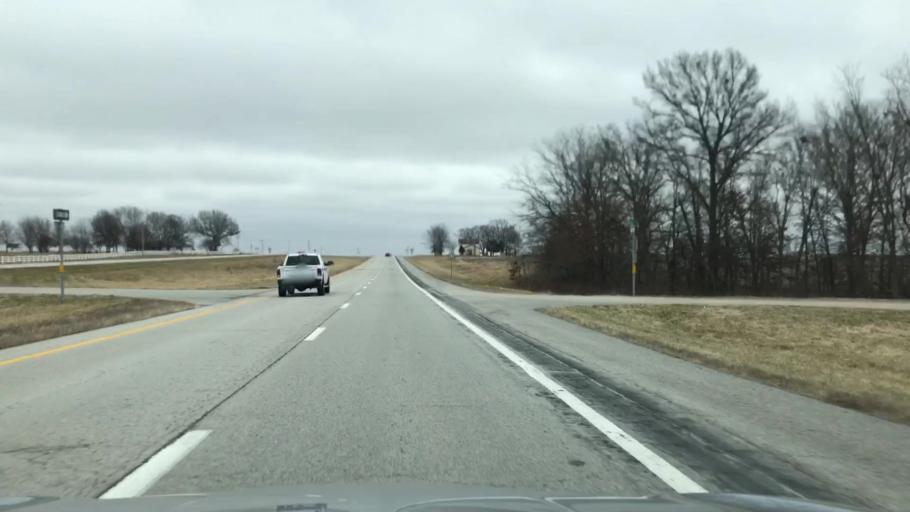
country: US
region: Missouri
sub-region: Linn County
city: Linneus
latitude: 39.7772
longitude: -93.3488
